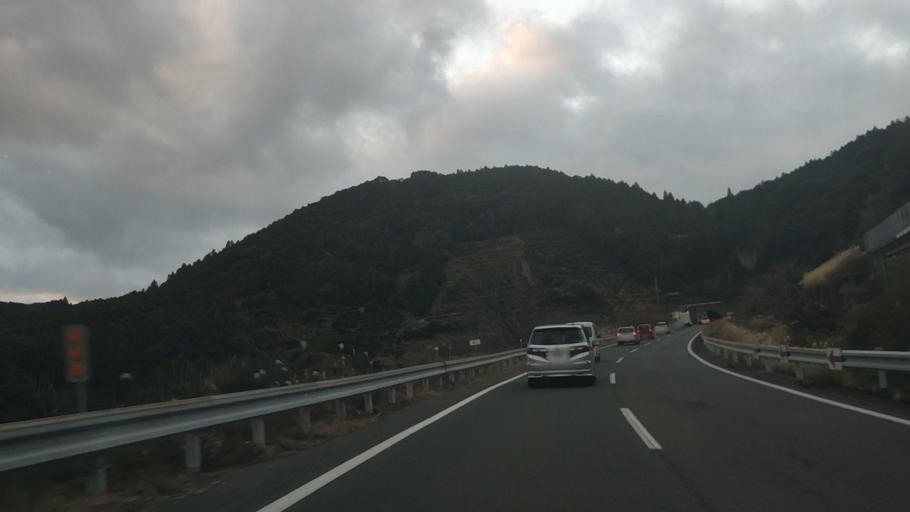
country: JP
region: Nagasaki
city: Obita
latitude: 32.8112
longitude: 129.9336
